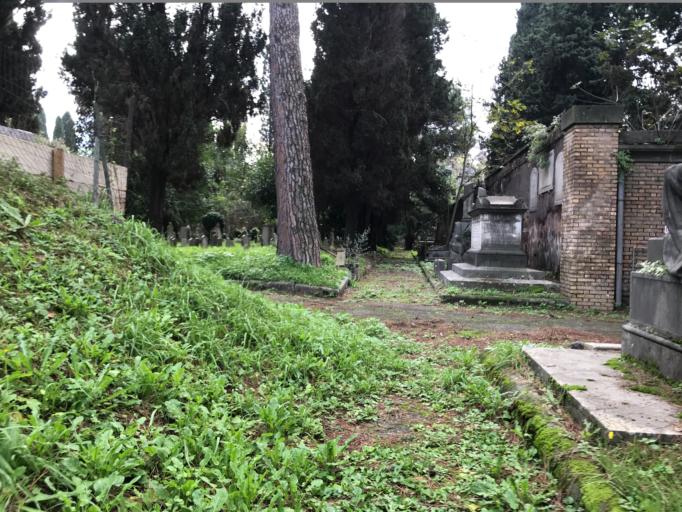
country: IT
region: Latium
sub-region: Citta metropolitana di Roma Capitale
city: Rome
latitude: 41.9077
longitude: 12.5279
